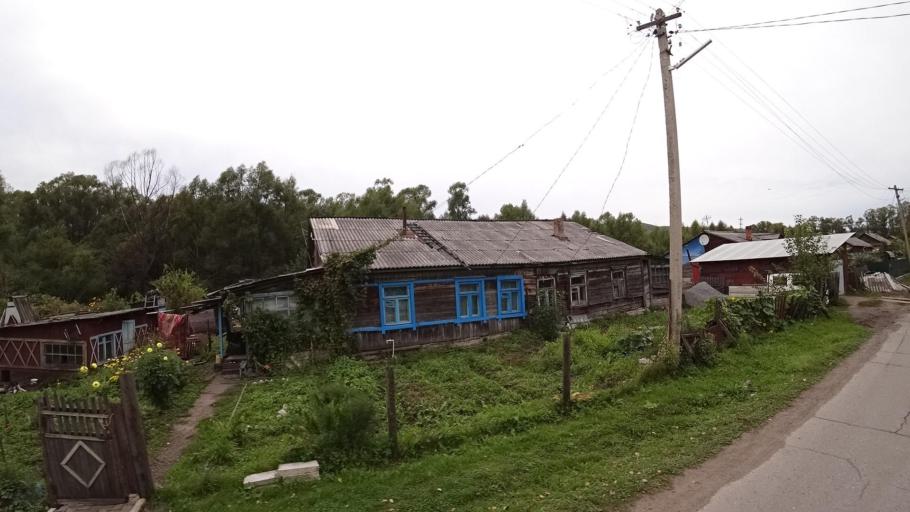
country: RU
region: Jewish Autonomous Oblast
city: Khingansk
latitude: 49.0263
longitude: 131.0532
